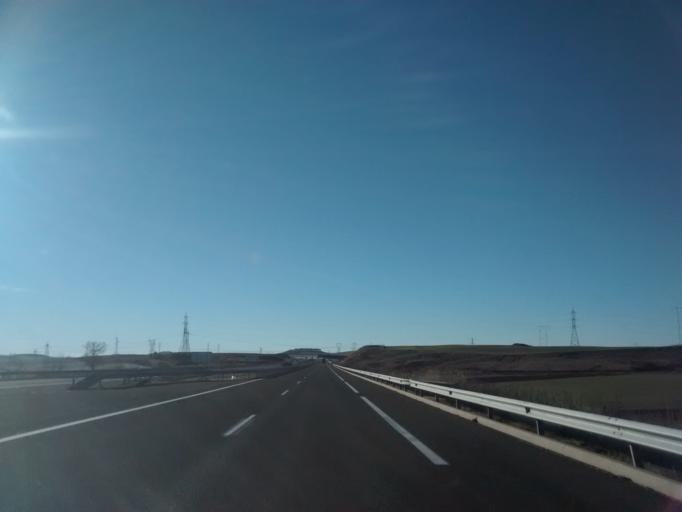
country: ES
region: Castille and Leon
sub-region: Provincia de Palencia
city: Herrera de Pisuerga
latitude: 42.6026
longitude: -4.3495
